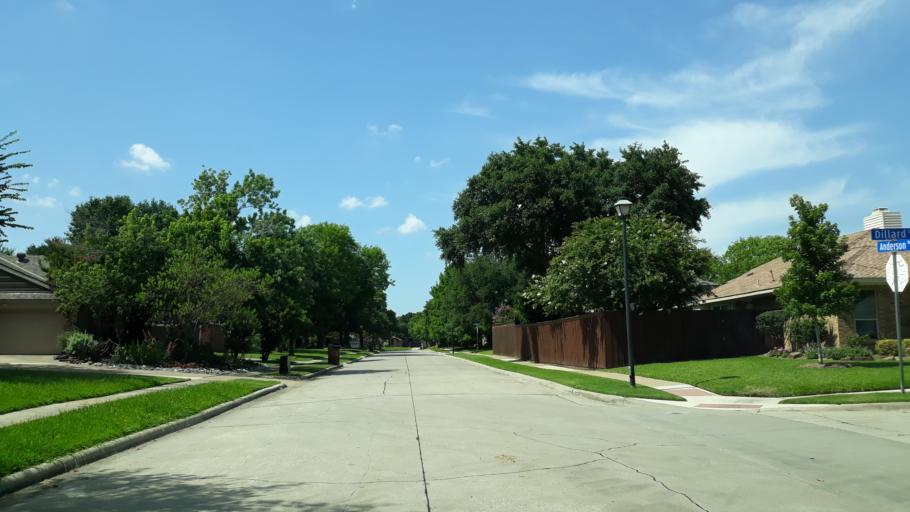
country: US
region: Texas
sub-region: Dallas County
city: Coppell
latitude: 32.9572
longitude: -97.0046
